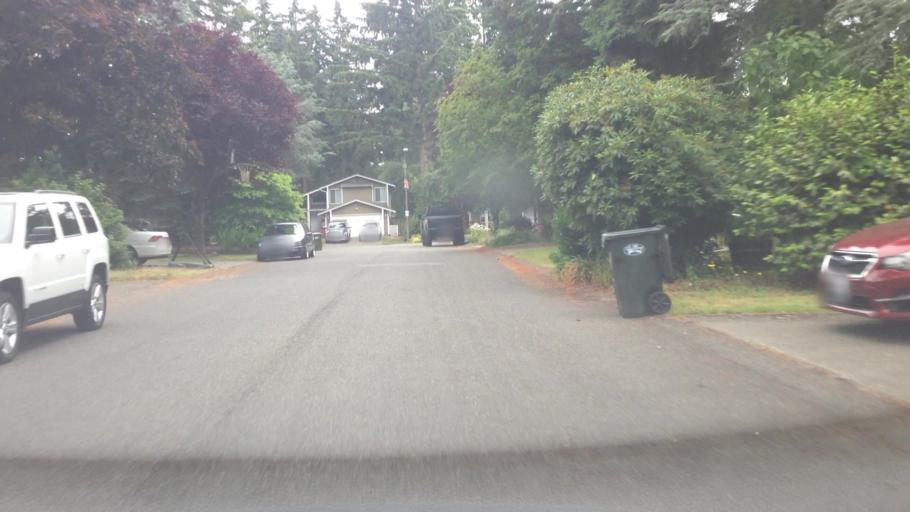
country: US
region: Washington
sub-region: Pierce County
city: South Hill
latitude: 47.1080
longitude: -122.2995
